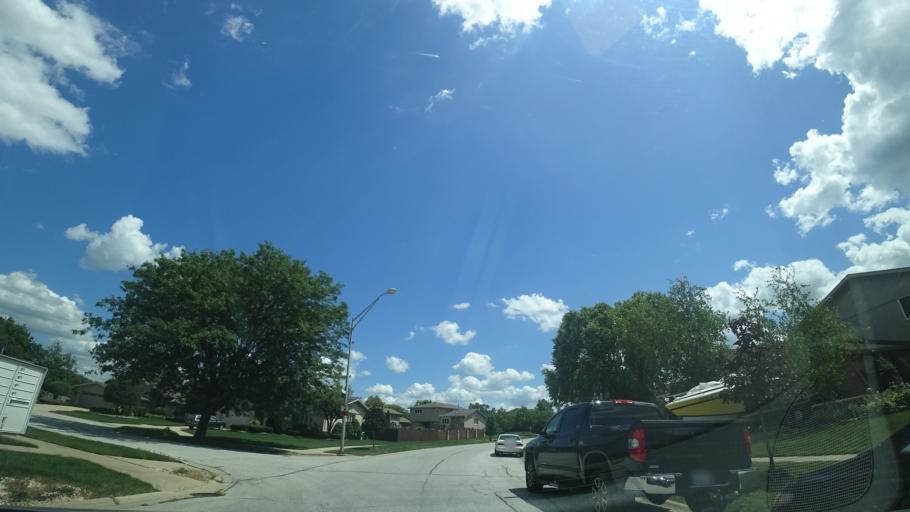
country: US
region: Illinois
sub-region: Will County
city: Homer Glen
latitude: 41.5732
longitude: -87.9044
